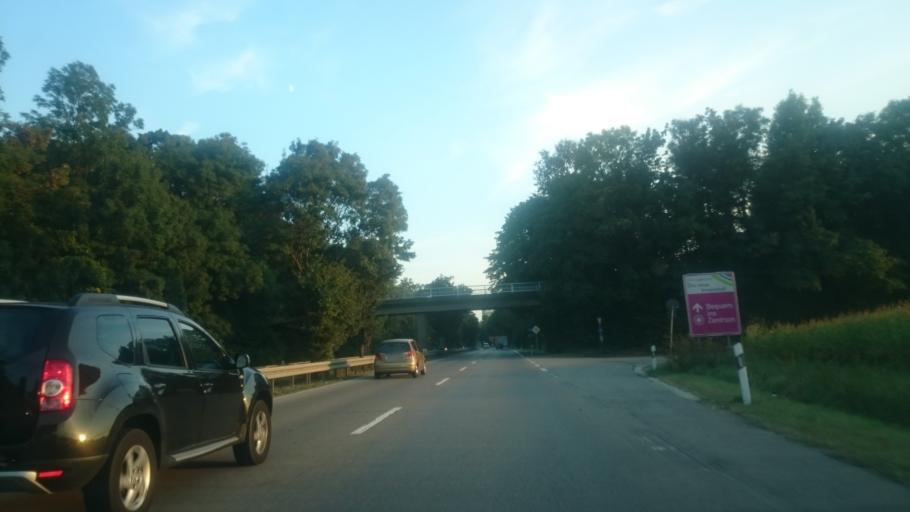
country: DE
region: Bavaria
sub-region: Swabia
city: Augsburg
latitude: 48.4038
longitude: 10.9202
